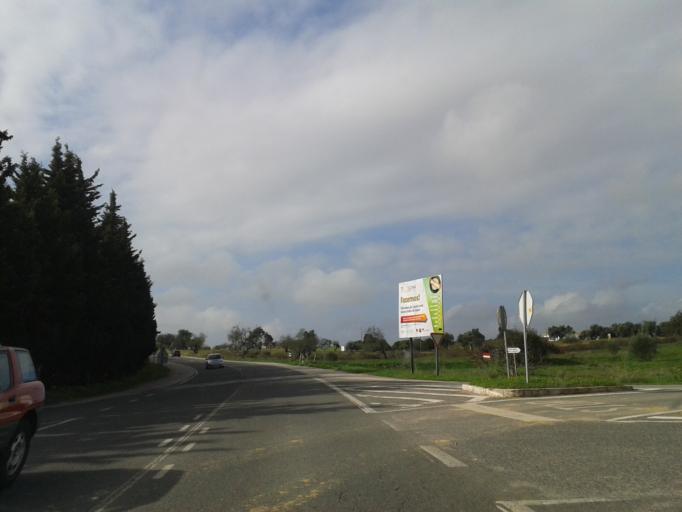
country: PT
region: Faro
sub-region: Tavira
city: Tavira
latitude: 37.1652
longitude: -7.5627
